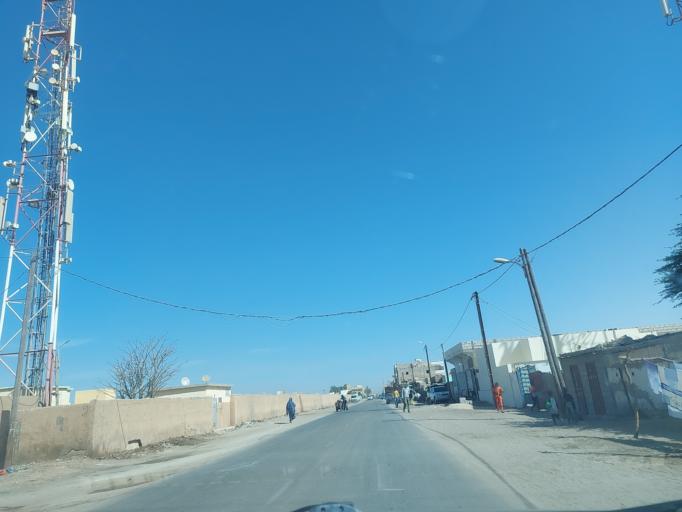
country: MR
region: Nouakchott
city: Nouakchott
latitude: 18.0695
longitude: -15.9947
